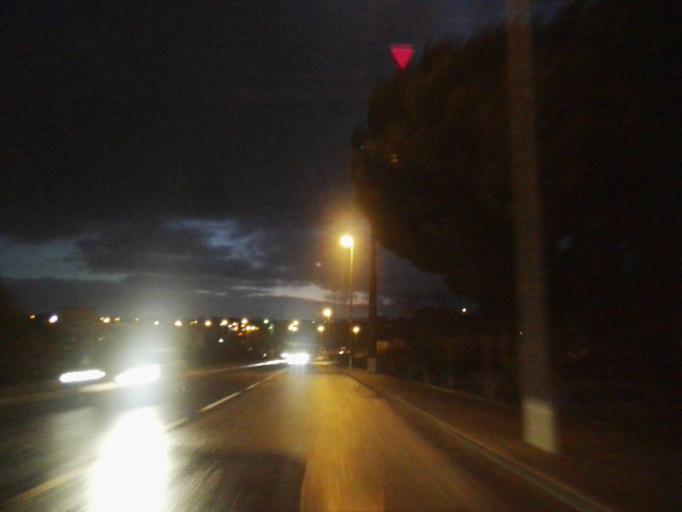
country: PT
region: Santarem
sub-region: Cartaxo
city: Cartaxo
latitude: 39.1678
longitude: -8.7971
